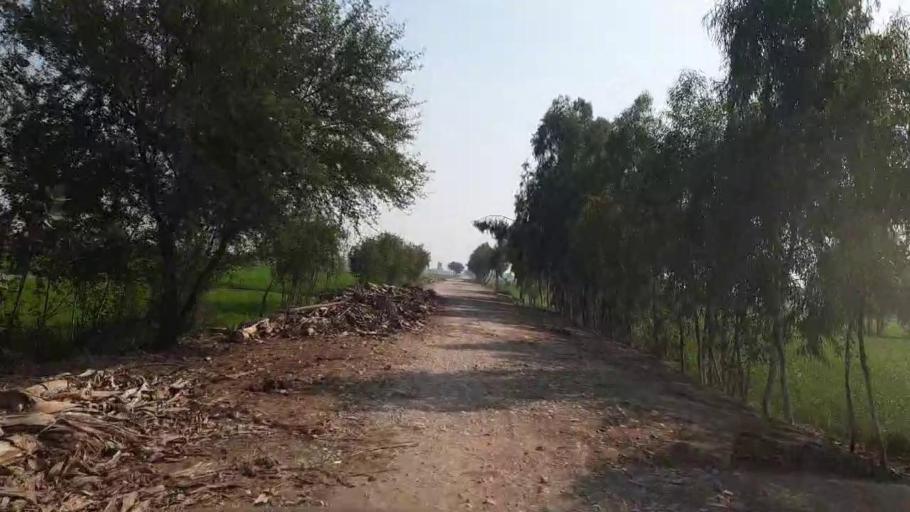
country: PK
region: Sindh
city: Bhit Shah
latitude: 25.7365
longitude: 68.5241
